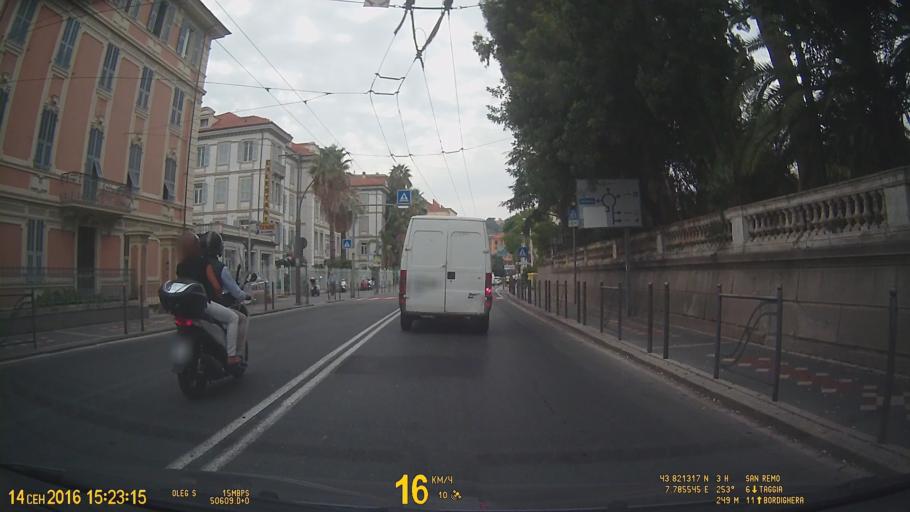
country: IT
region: Liguria
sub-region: Provincia di Imperia
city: San Remo
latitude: 43.8216
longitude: 7.7879
